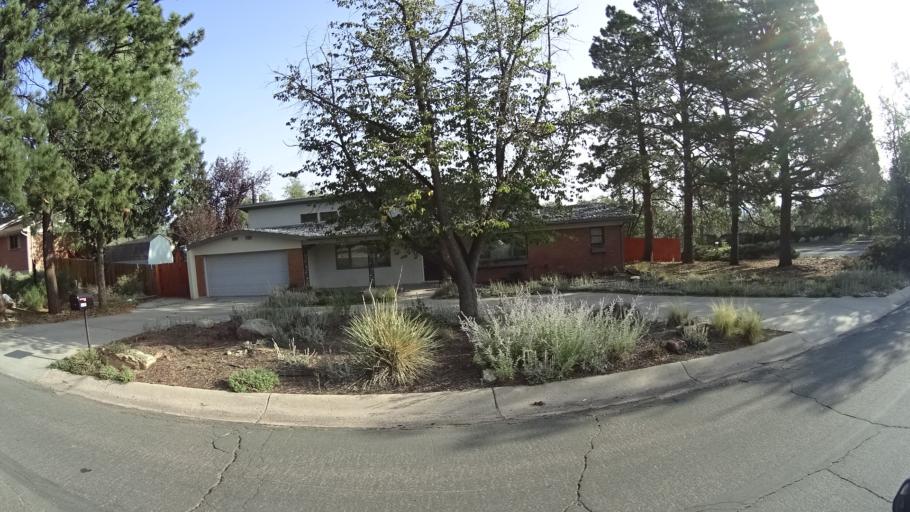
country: US
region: Colorado
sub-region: El Paso County
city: Colorado Springs
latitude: 38.8153
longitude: -104.8600
